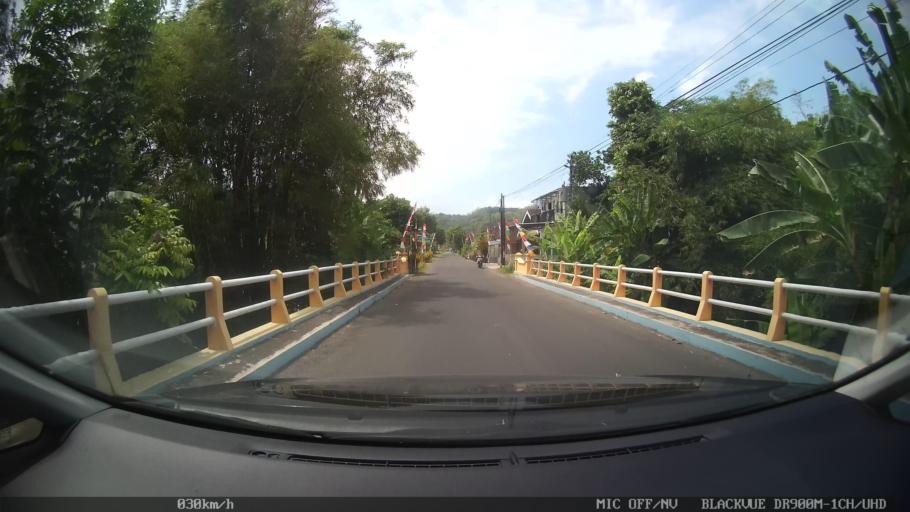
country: ID
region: Central Java
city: Candi Prambanan
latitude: -7.8142
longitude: 110.4966
